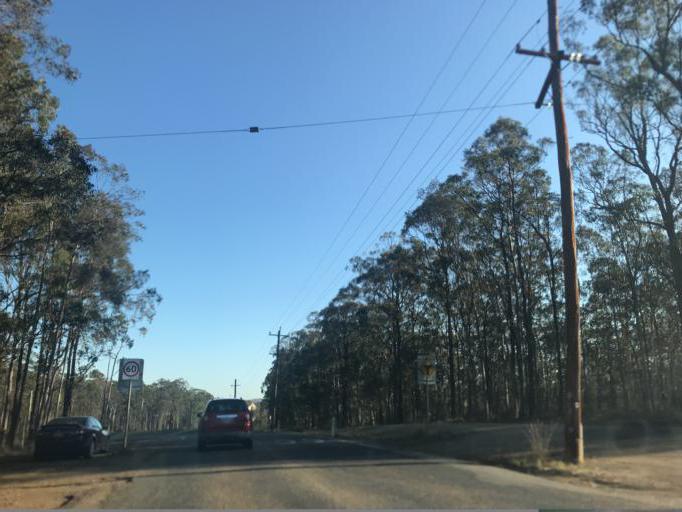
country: AU
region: New South Wales
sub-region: Cessnock
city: Cessnock
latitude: -32.8769
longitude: 151.3112
